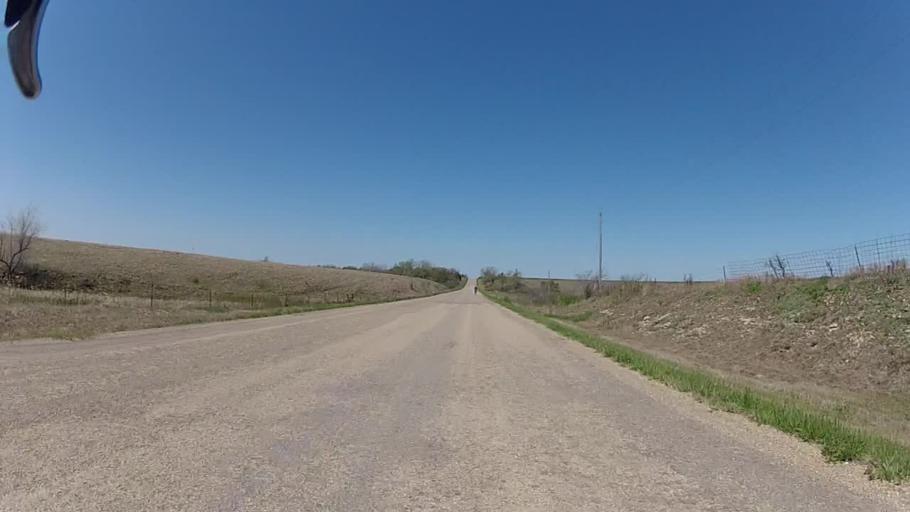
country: US
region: Kansas
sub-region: Riley County
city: Manhattan
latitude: 38.9716
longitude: -96.5398
